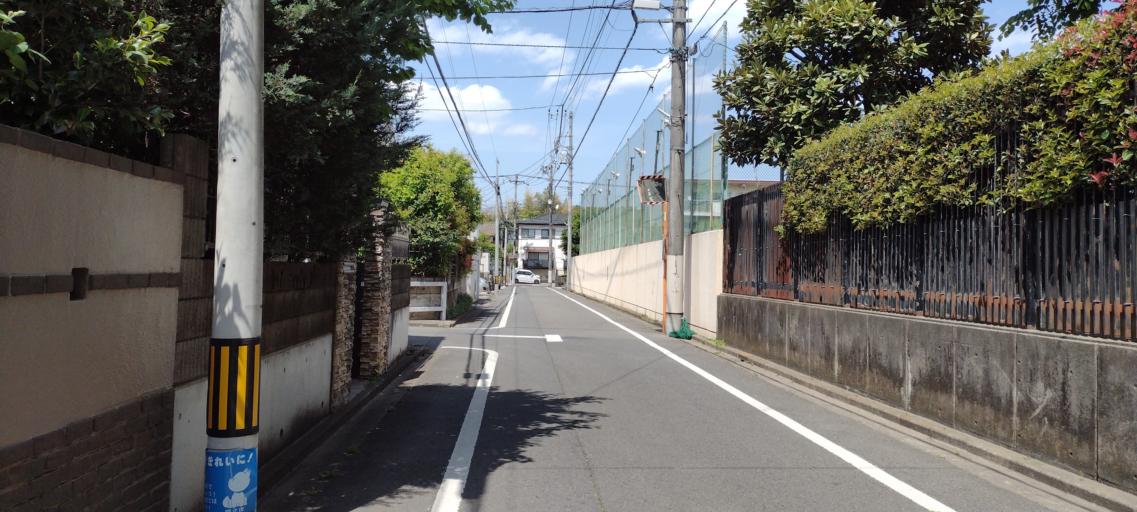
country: JP
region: Tokyo
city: Kokubunji
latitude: 35.6896
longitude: 139.4429
